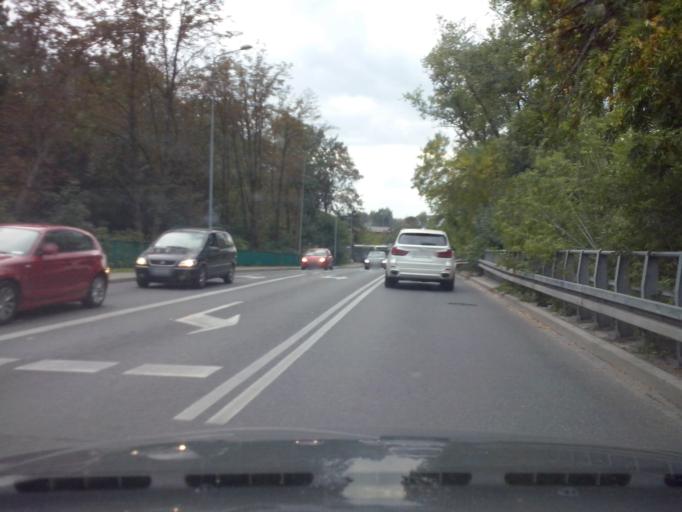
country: PL
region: Lesser Poland Voivodeship
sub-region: Krakow
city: Krakow
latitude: 50.0316
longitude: 19.9485
